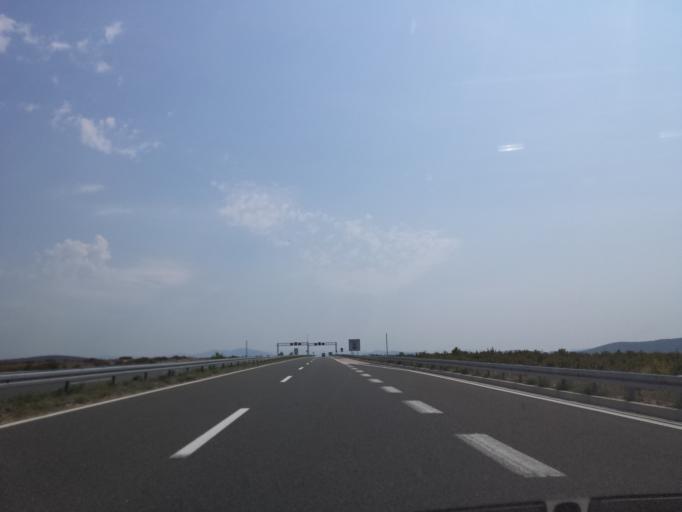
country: HR
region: Sibensko-Kniniska
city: Zaton
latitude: 43.8865
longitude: 15.7919
